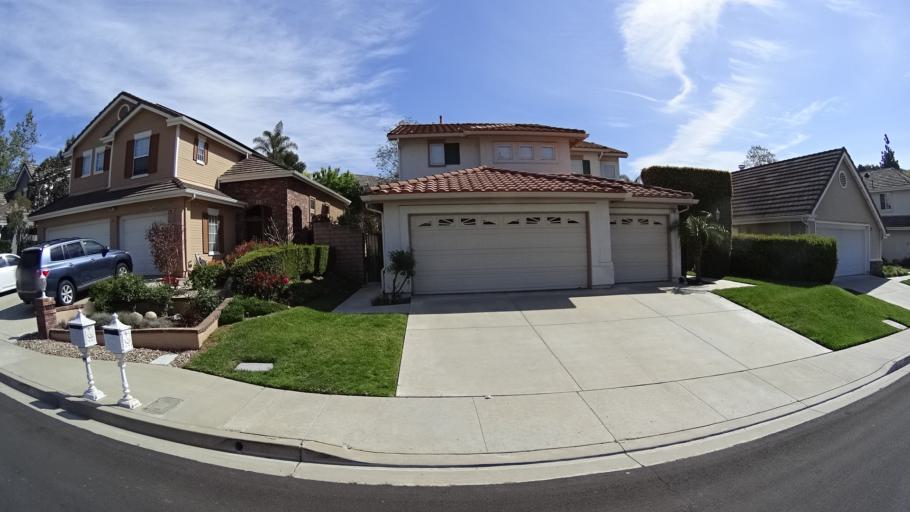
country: US
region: California
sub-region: Ventura County
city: Thousand Oaks
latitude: 34.2166
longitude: -118.8354
